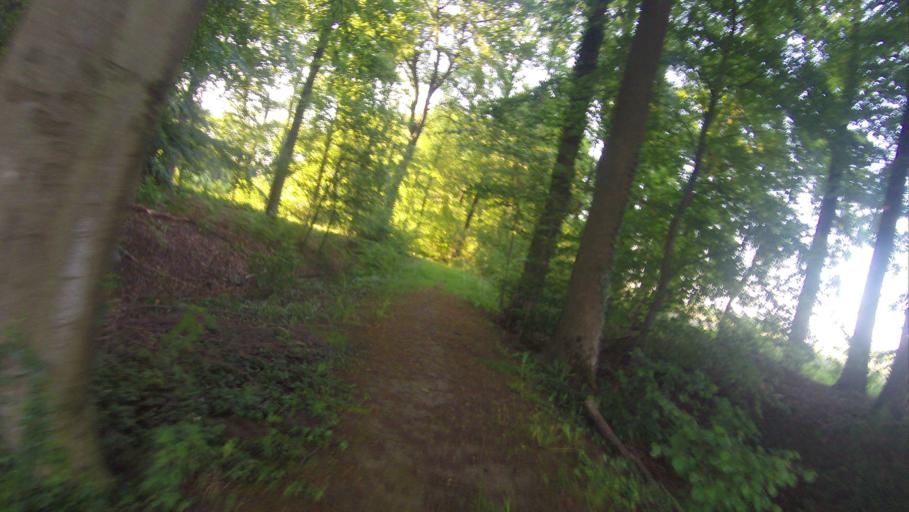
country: NL
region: Gelderland
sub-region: Gemeente Lochem
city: Lochem
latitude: 52.1172
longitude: 6.3884
